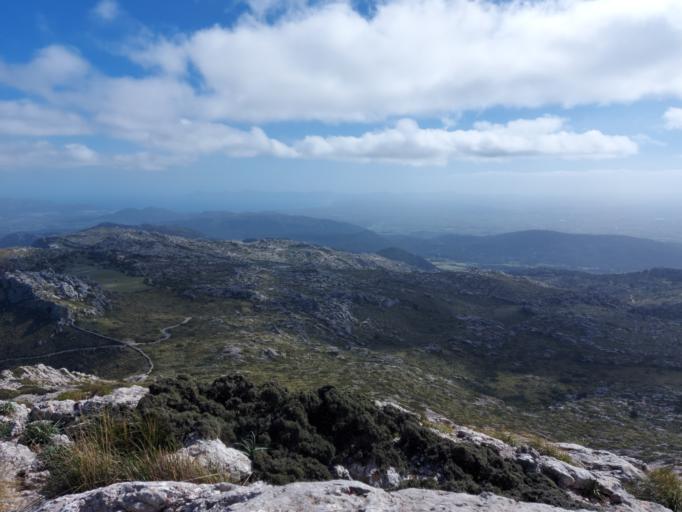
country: ES
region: Balearic Islands
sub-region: Illes Balears
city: Campanet
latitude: 39.8439
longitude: 2.9494
